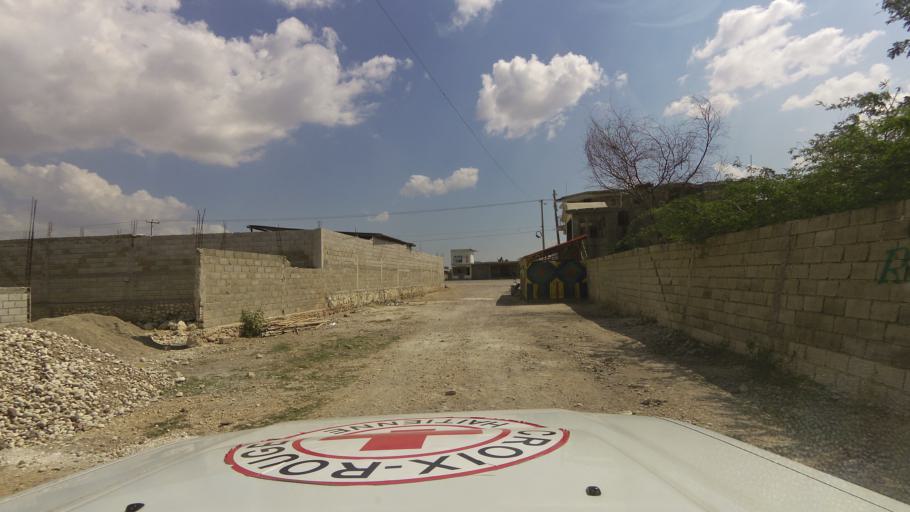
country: HT
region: Ouest
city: Croix des Bouquets
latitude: 18.6405
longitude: -72.2632
